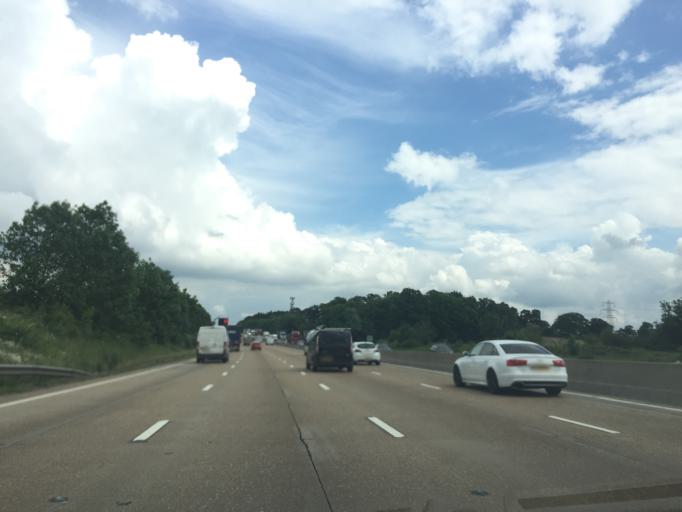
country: GB
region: England
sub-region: Hertfordshire
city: Cuffley
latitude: 51.6899
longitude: -0.0945
